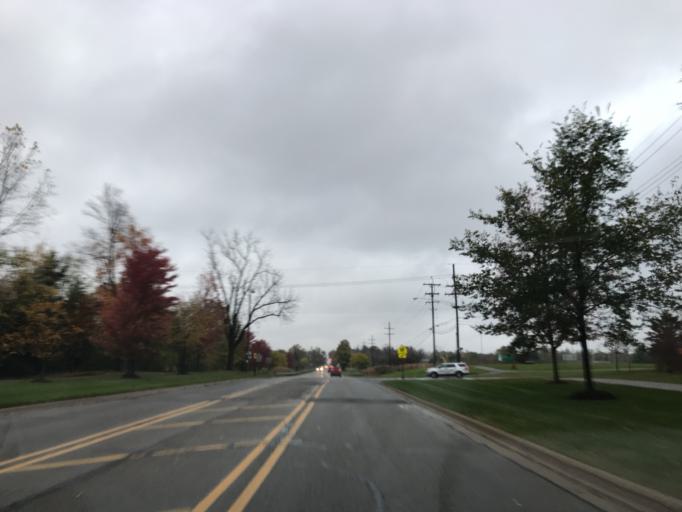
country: US
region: Michigan
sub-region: Oakland County
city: Wixom
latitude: 42.4785
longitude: -83.5346
